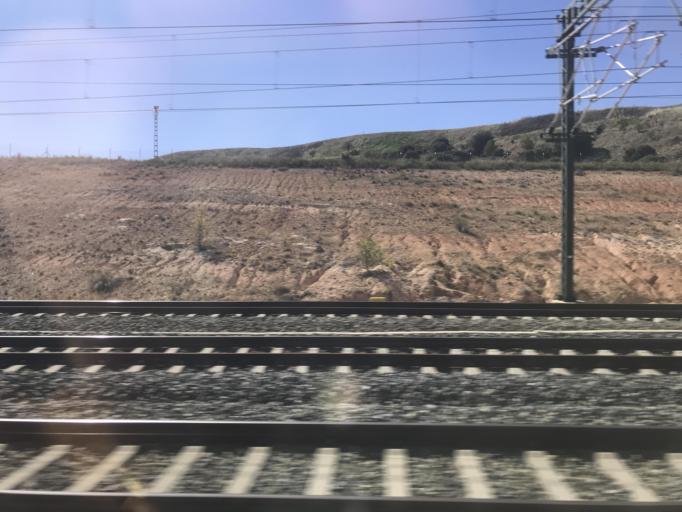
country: ES
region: Castille-La Mancha
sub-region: Provincia de Cuenca
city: Cuenca
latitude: 40.0359
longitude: -2.1453
